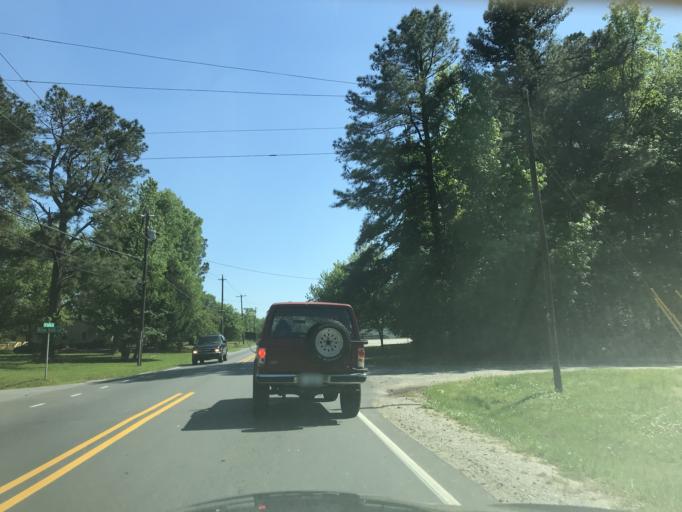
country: US
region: North Carolina
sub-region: Wake County
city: Garner
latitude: 35.7198
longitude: -78.6243
